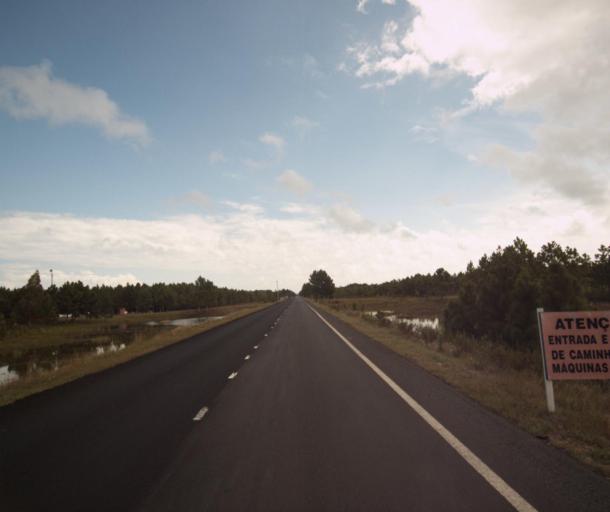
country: BR
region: Rio Grande do Sul
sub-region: Tapes
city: Tapes
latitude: -31.4238
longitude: -51.1820
